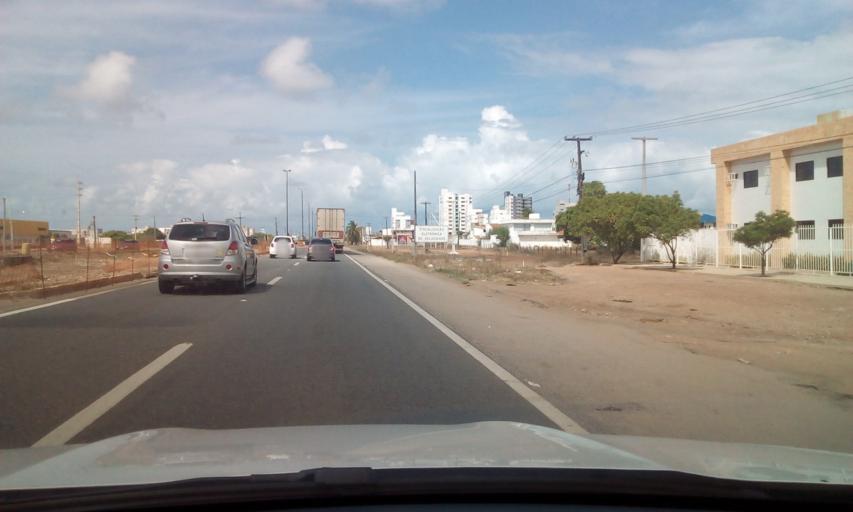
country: BR
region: Paraiba
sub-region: Cabedelo
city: Cabedelo
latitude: -7.0408
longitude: -34.8451
